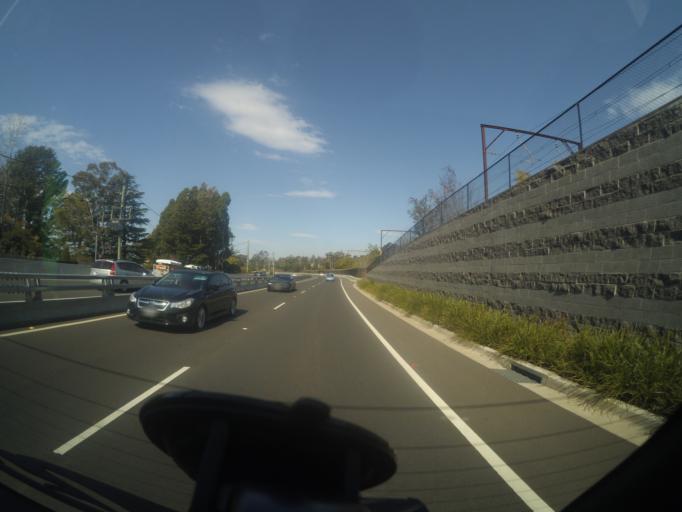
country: AU
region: New South Wales
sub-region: Blue Mountains Municipality
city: Hazelbrook
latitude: -33.7314
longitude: 150.4646
